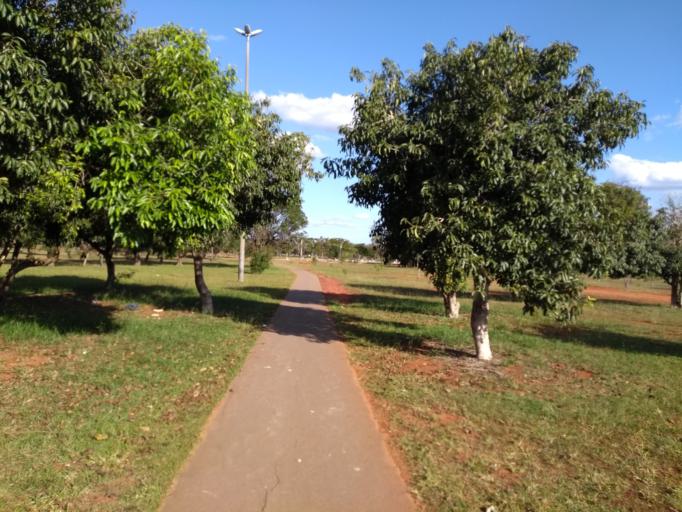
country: BR
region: Federal District
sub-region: Brasilia
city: Brasilia
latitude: -15.8079
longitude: -47.9191
